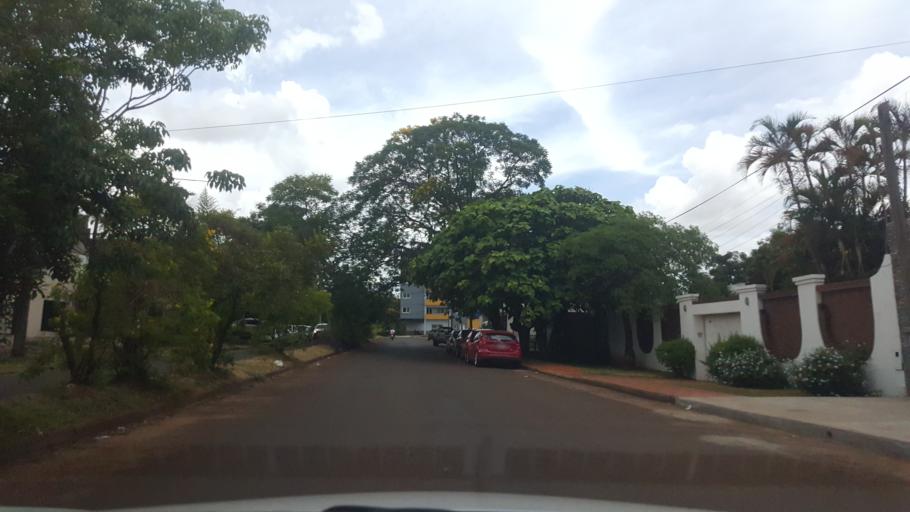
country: AR
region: Misiones
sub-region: Departamento de Capital
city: Posadas
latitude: -27.3999
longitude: -55.8935
